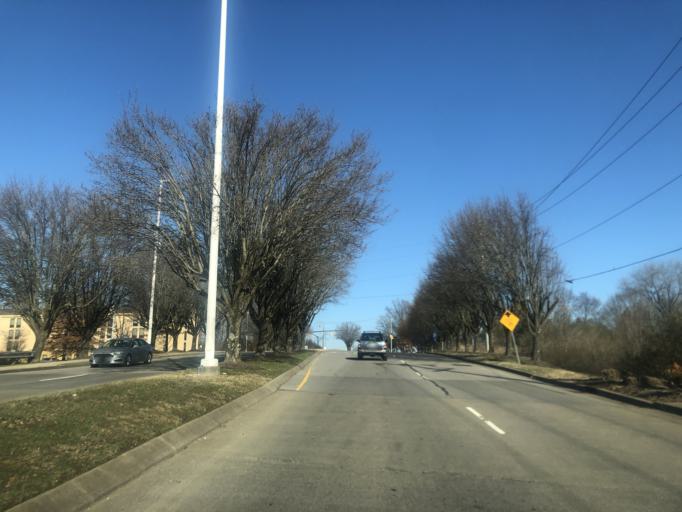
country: US
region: Tennessee
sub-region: Rutherford County
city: La Vergne
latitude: 36.0436
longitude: -86.6469
